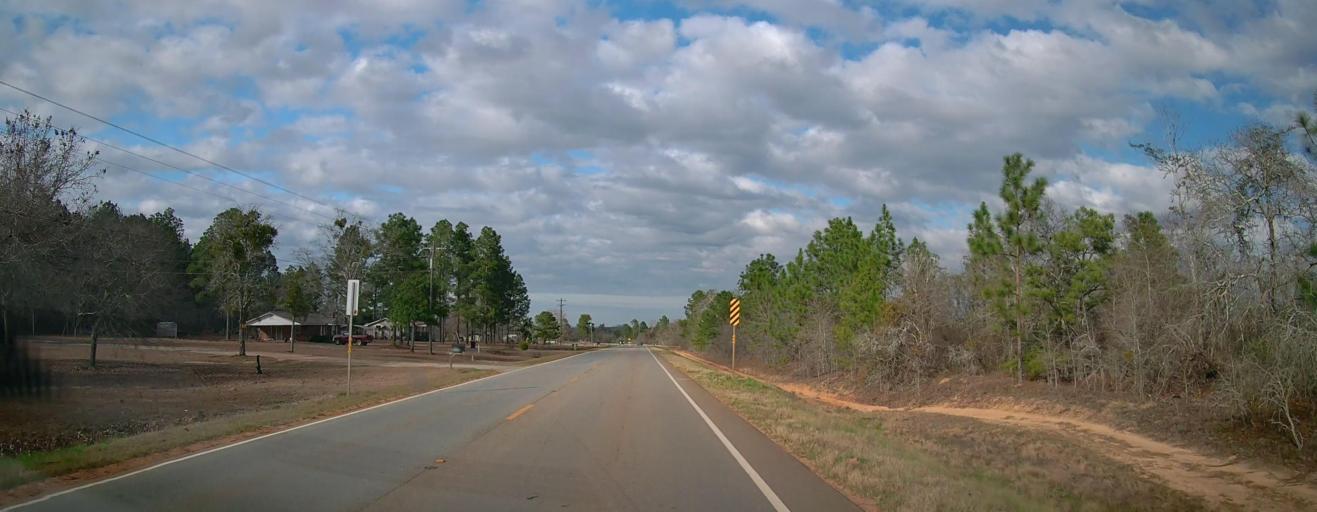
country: US
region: Georgia
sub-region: Marion County
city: Buena Vista
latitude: 32.4469
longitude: -84.5366
